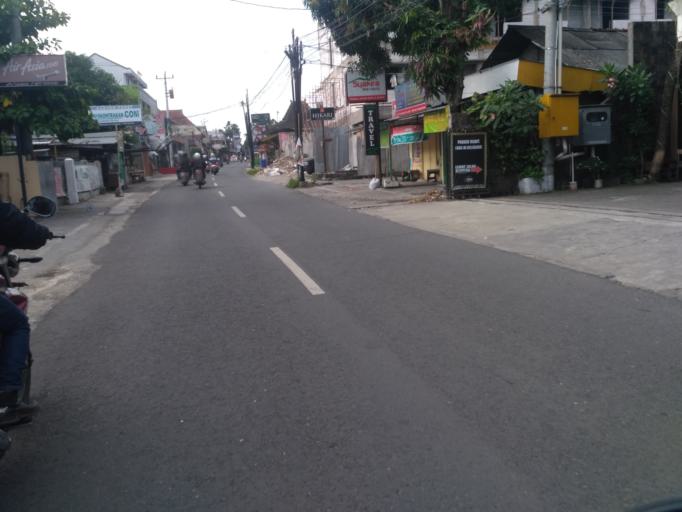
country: ID
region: Daerah Istimewa Yogyakarta
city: Depok
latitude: -7.7650
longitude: 110.4058
